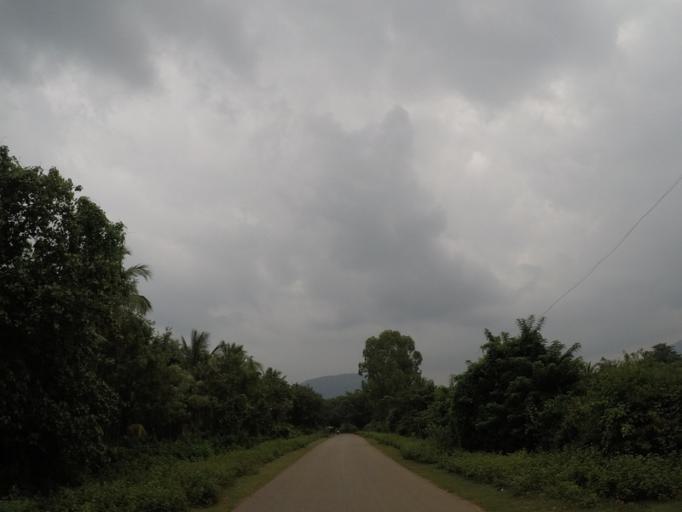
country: IN
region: Karnataka
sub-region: Chikmagalur
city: Tarikere
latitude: 13.5904
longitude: 75.8319
